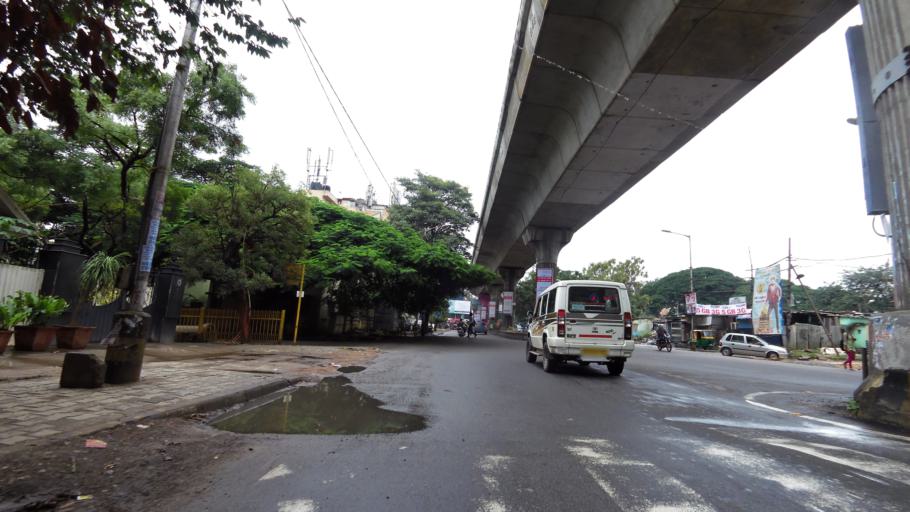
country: IN
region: Karnataka
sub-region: Bangalore Urban
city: Bangalore
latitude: 12.9822
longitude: 77.6406
